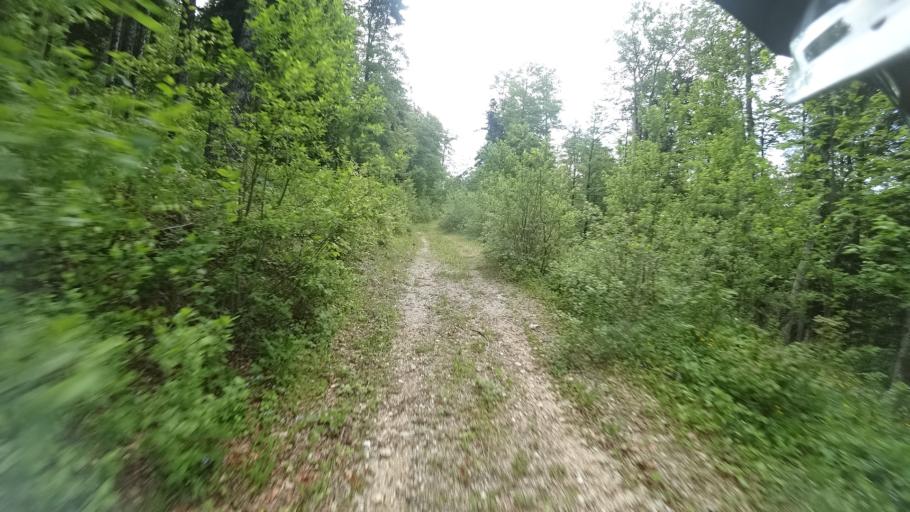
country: BA
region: Federation of Bosnia and Herzegovina
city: Orasac
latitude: 44.5702
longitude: 15.8681
